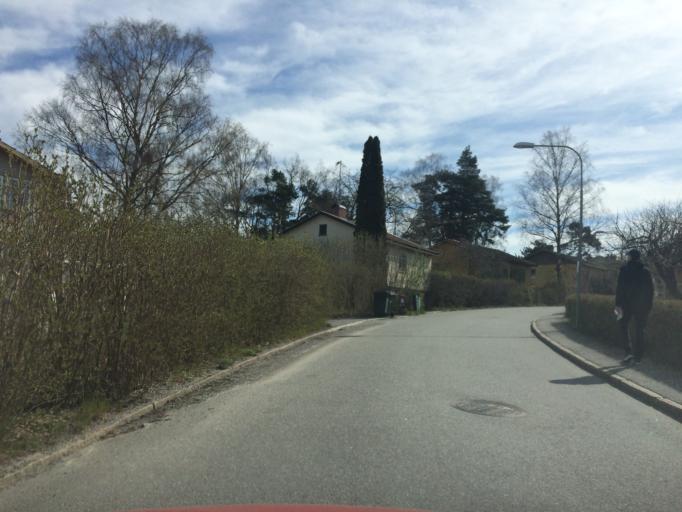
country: SE
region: Stockholm
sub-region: Huddinge Kommun
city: Huddinge
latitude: 59.2837
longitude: 17.9862
